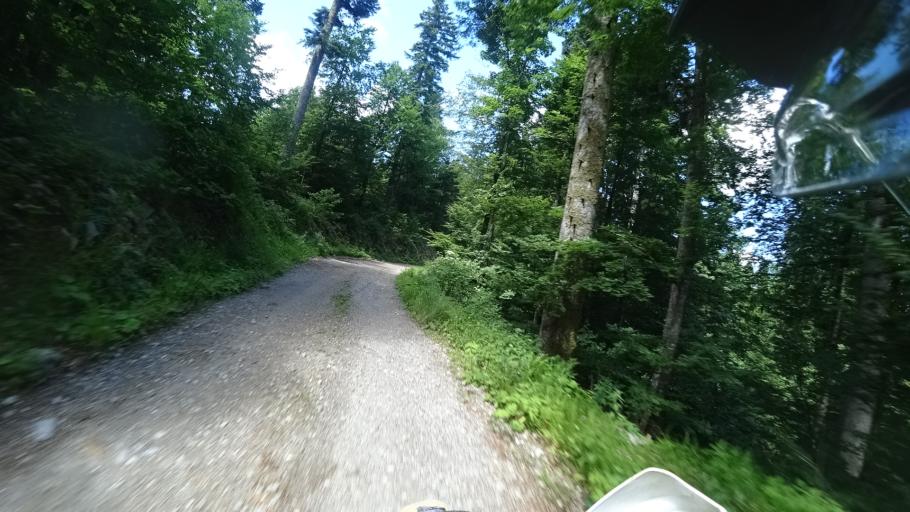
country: HR
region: Primorsko-Goranska
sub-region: Grad Delnice
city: Delnice
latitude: 45.4331
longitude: 14.7526
